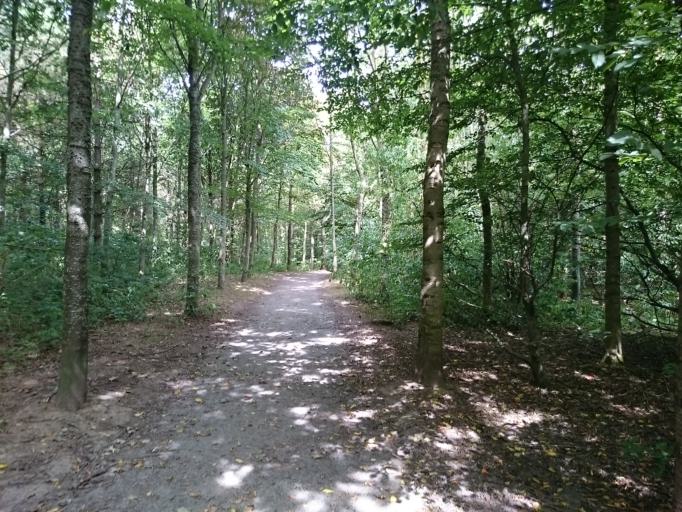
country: FR
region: Lower Normandy
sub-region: Departement du Calvados
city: Ifs
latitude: 49.1441
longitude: -0.3586
